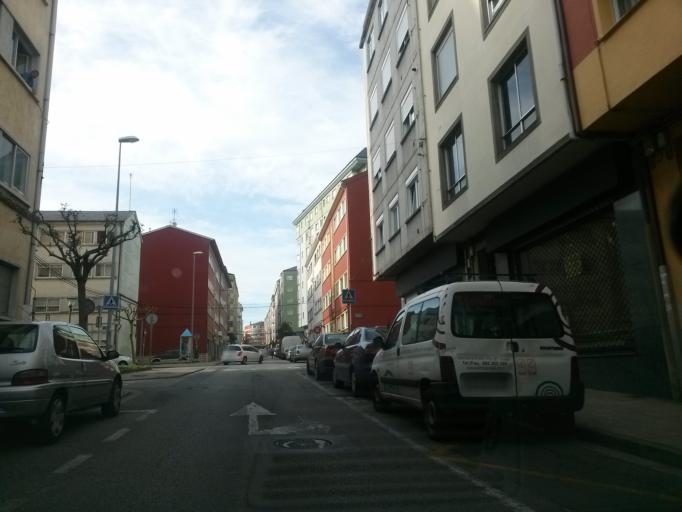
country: ES
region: Galicia
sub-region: Provincia de Lugo
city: Lugo
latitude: 43.0148
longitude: -7.5665
